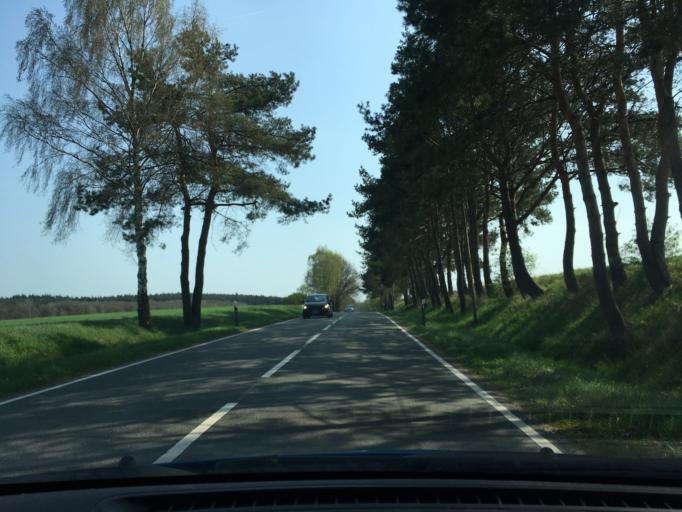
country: DE
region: Lower Saxony
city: Sudergellersen
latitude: 53.2027
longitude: 10.3014
